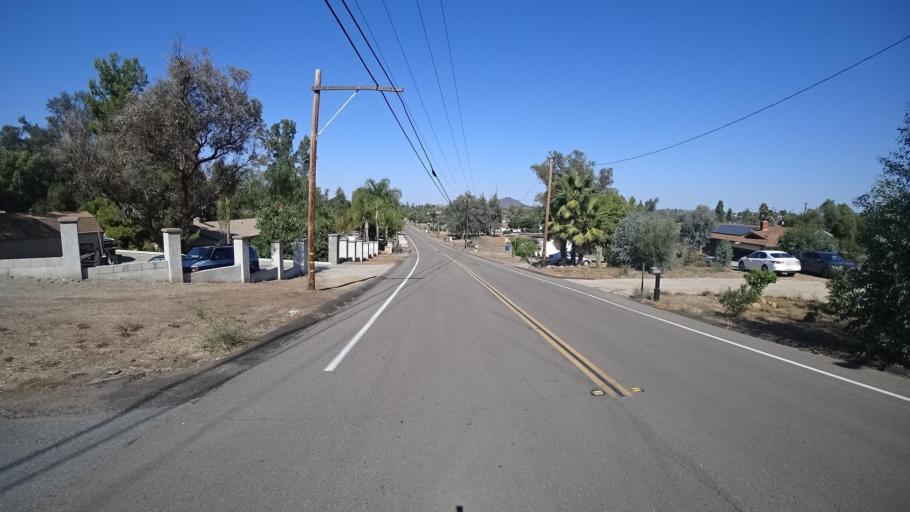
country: US
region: California
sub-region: San Diego County
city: Granite Hills
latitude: 32.7933
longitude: -116.9107
